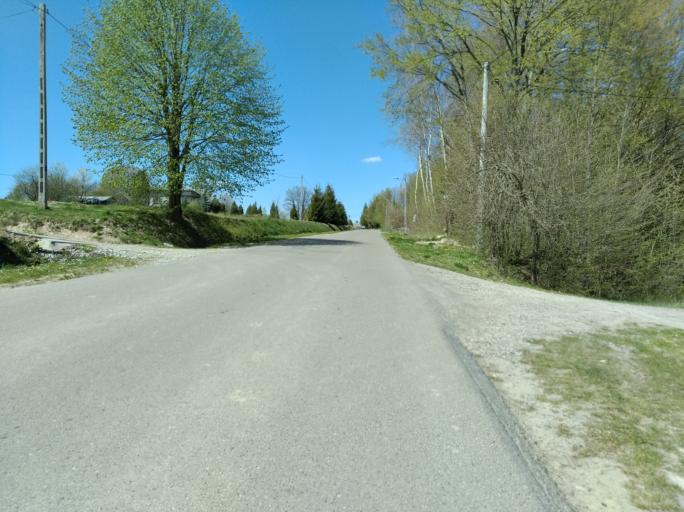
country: PL
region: Subcarpathian Voivodeship
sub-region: Powiat brzozowski
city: Jablonka
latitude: 49.7235
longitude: 22.1158
